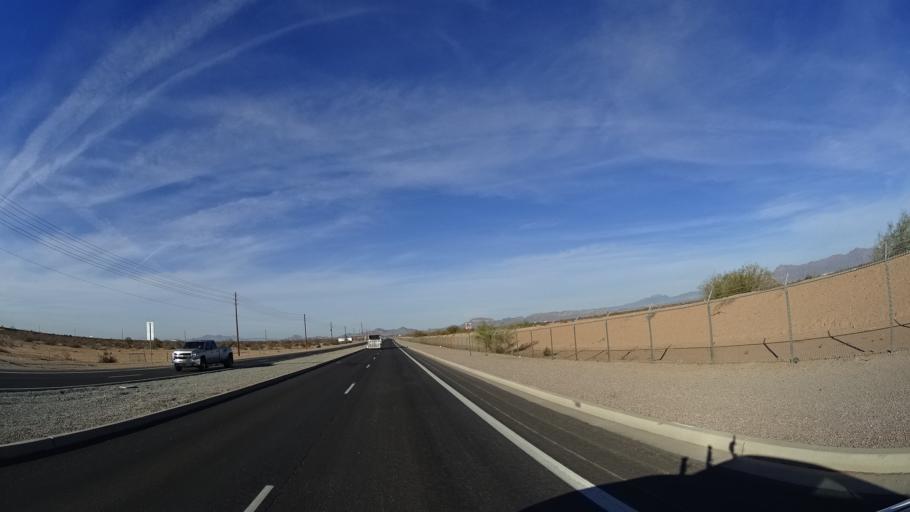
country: US
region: Arizona
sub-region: Maricopa County
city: Queen Creek
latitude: 33.3310
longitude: -111.6356
